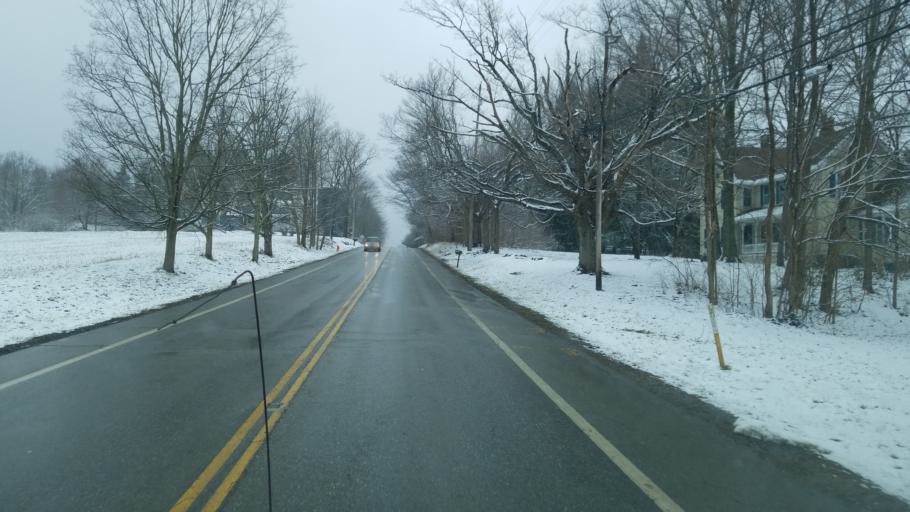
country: US
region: Ohio
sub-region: Portage County
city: Hiram
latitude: 41.3098
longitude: -81.1568
